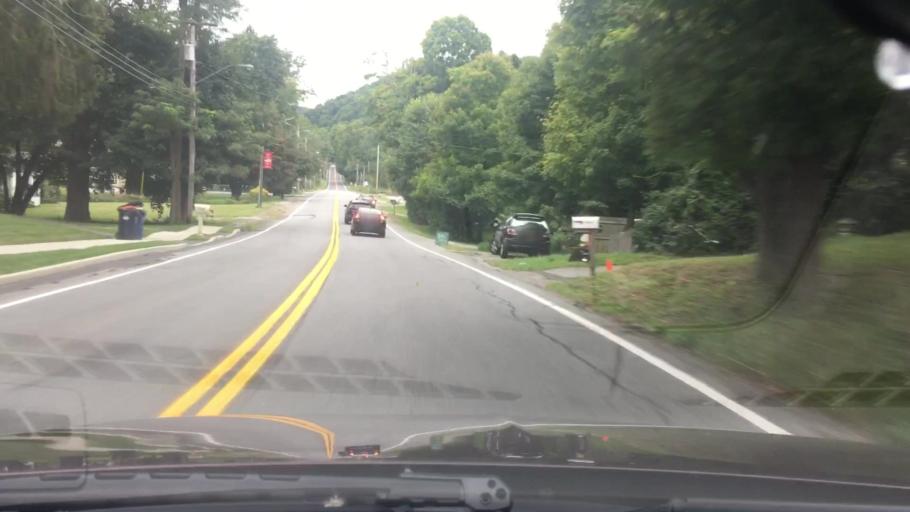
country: US
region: New York
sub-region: Dutchess County
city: Dover Plains
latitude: 41.8488
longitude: -73.5594
